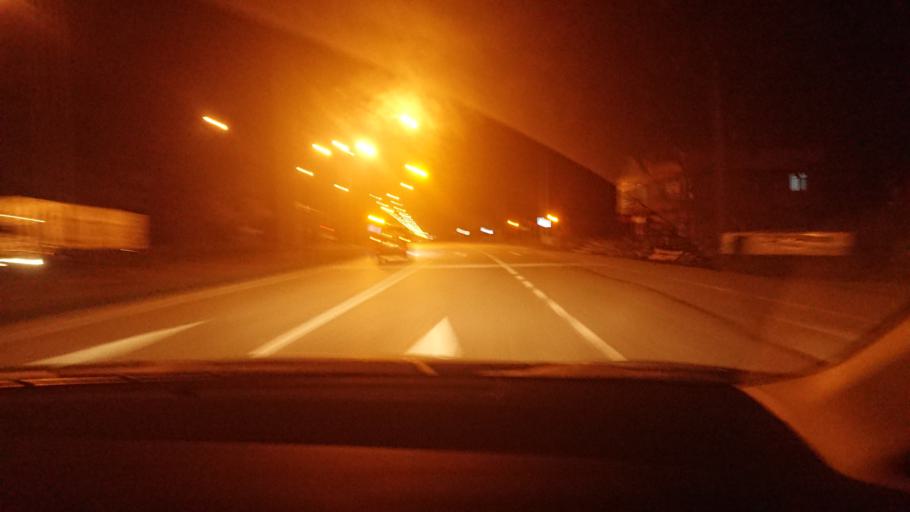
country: TR
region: Ordu
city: Ikizce
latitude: 41.1642
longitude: 37.0732
